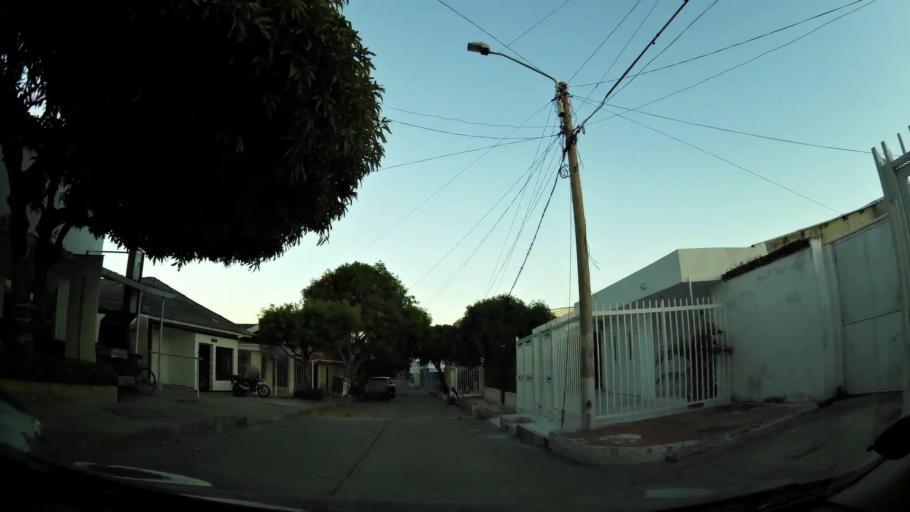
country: CO
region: Atlantico
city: Barranquilla
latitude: 10.9749
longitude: -74.8075
